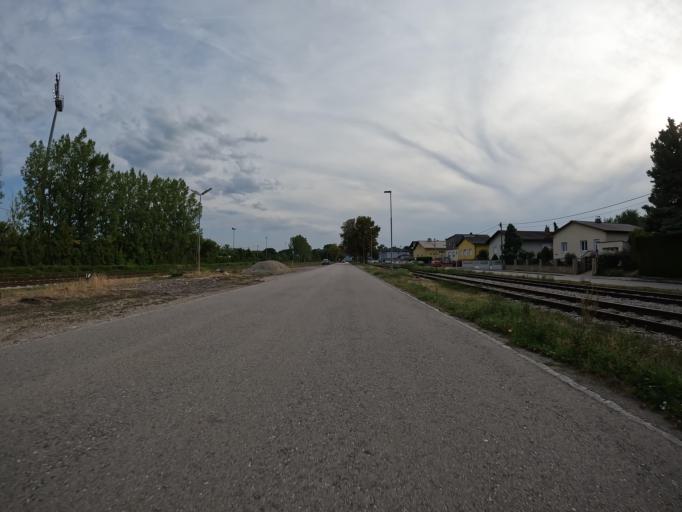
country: AT
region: Lower Austria
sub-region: Politischer Bezirk Baden
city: Traiskirchen
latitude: 48.0172
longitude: 16.3025
